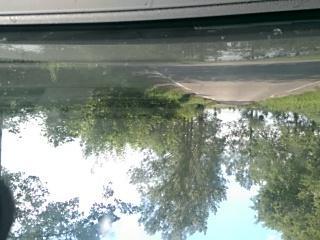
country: PL
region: Podlasie
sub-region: Powiat suwalski
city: Filipow
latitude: 54.1807
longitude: 22.5885
